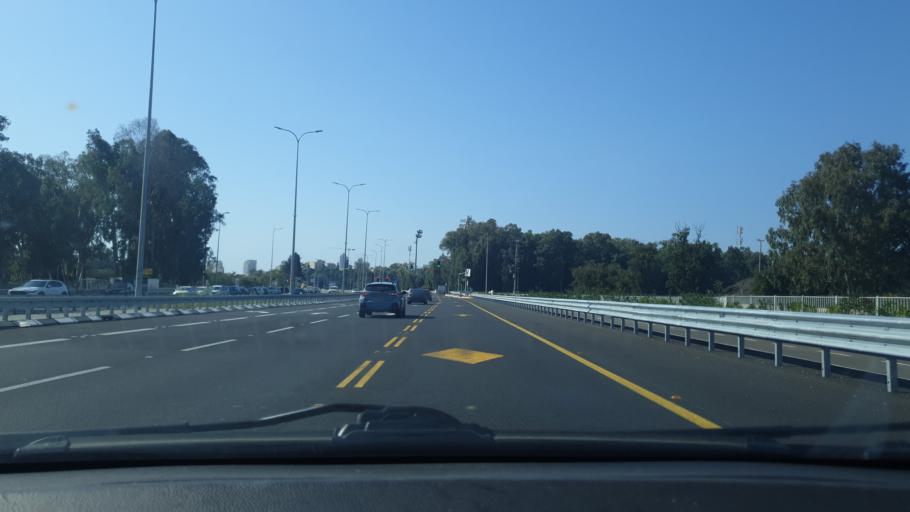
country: IL
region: Tel Aviv
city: Azor
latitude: 32.0429
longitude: 34.8190
